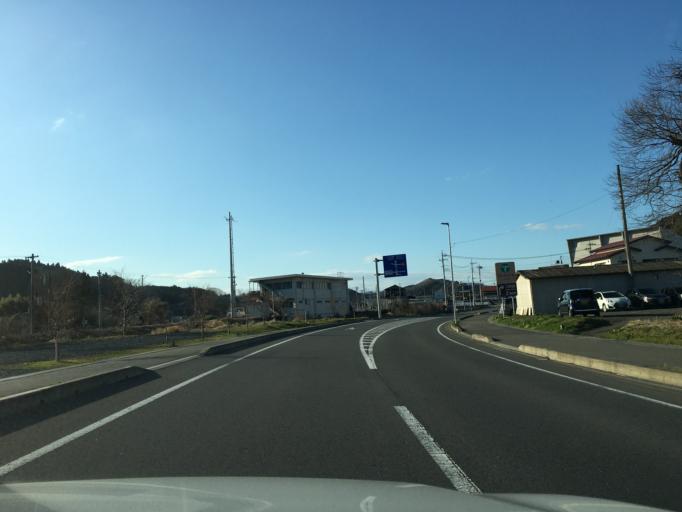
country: JP
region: Ibaraki
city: Daigo
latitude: 36.7692
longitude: 140.3525
